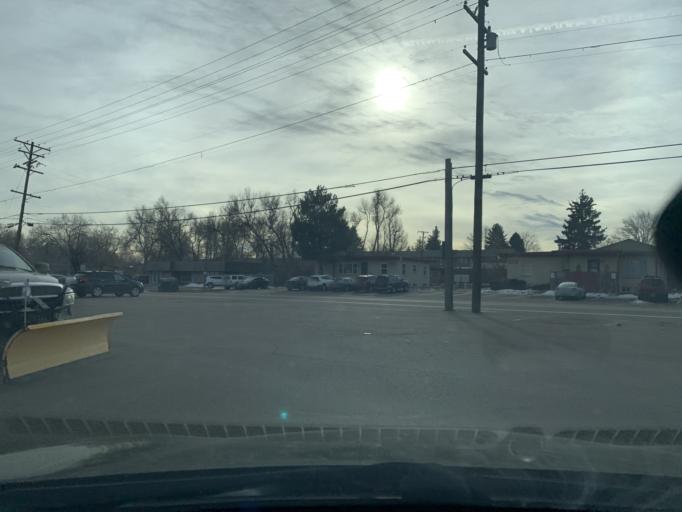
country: US
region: Colorado
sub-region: Jefferson County
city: Edgewater
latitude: 39.7477
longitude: -105.0802
